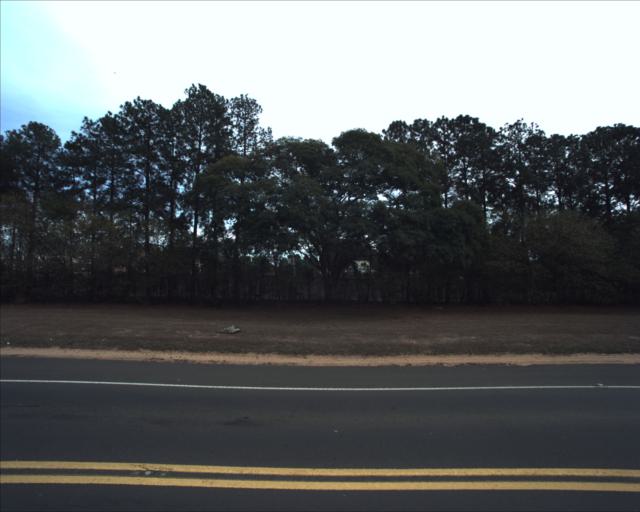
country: BR
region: Sao Paulo
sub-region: Sorocaba
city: Sorocaba
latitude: -23.4000
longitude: -47.5165
